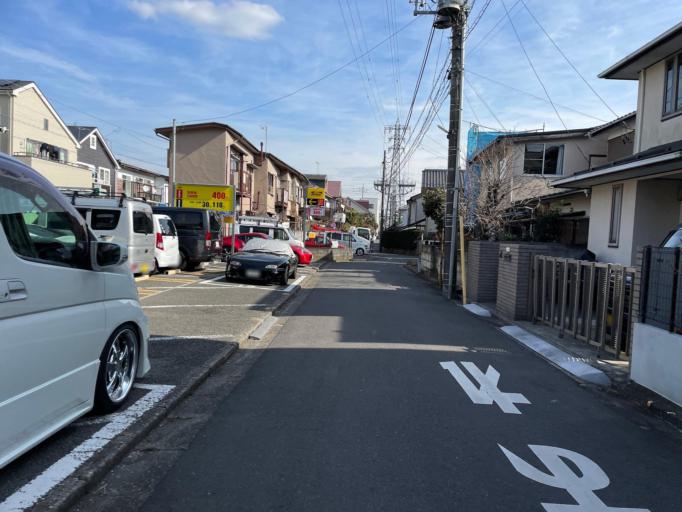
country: JP
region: Tokyo
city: Kamirenjaku
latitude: 35.6905
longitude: 139.5363
